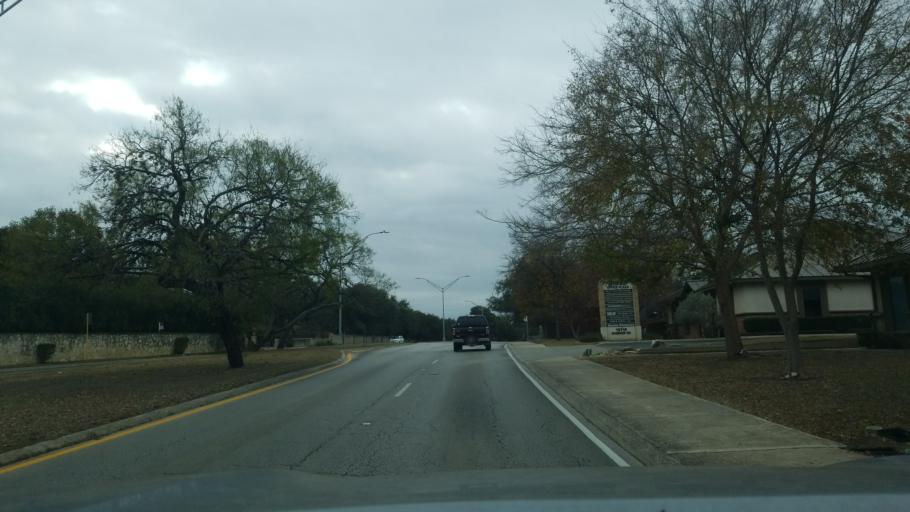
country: US
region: Texas
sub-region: Bexar County
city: Shavano Park
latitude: 29.6009
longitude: -98.5228
